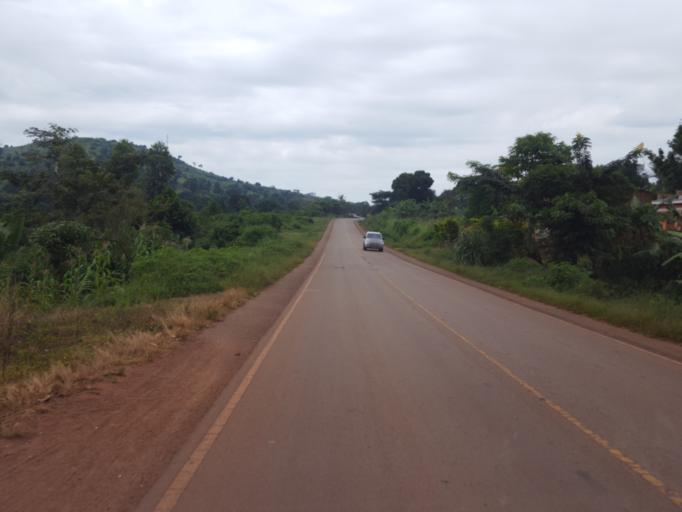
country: UG
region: Central Region
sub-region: Mityana District
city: Mityana
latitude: 0.6557
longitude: 32.0935
